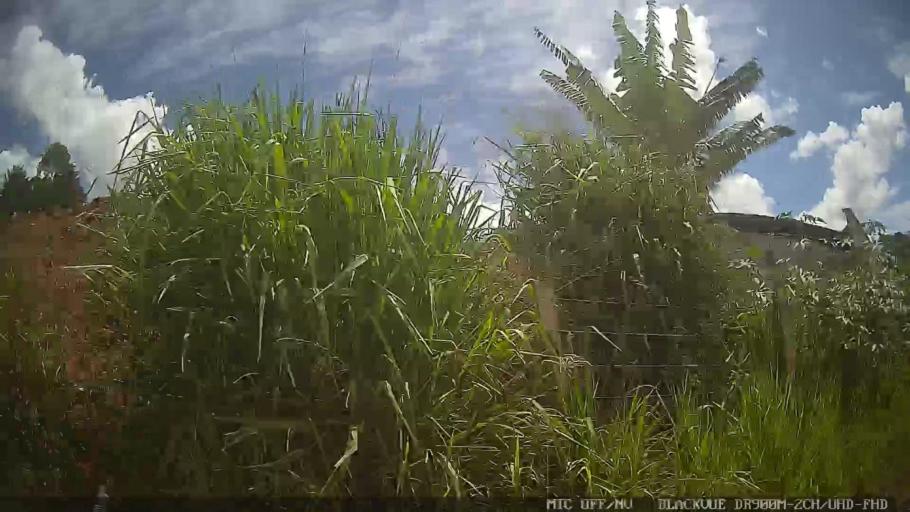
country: BR
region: Minas Gerais
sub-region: Extrema
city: Extrema
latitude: -22.7359
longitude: -46.3785
